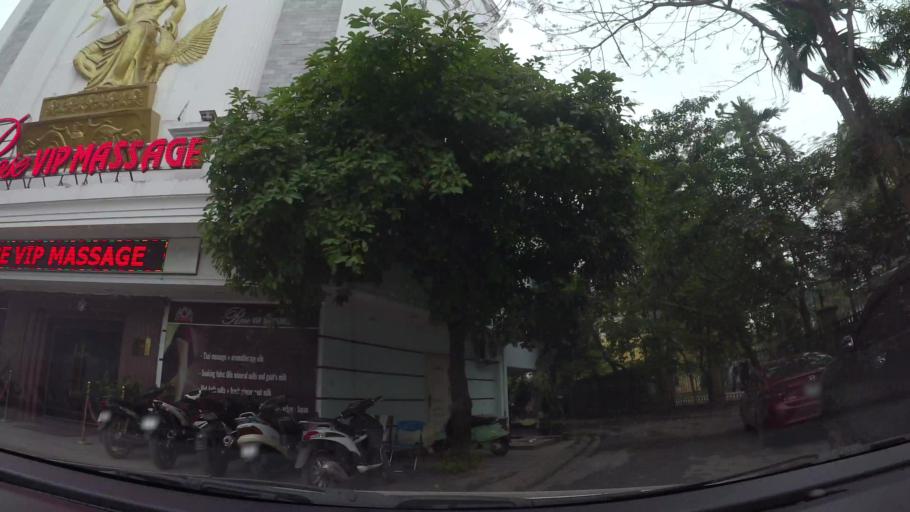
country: VN
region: Ha Noi
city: Tay Ho
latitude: 21.0770
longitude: 105.8200
